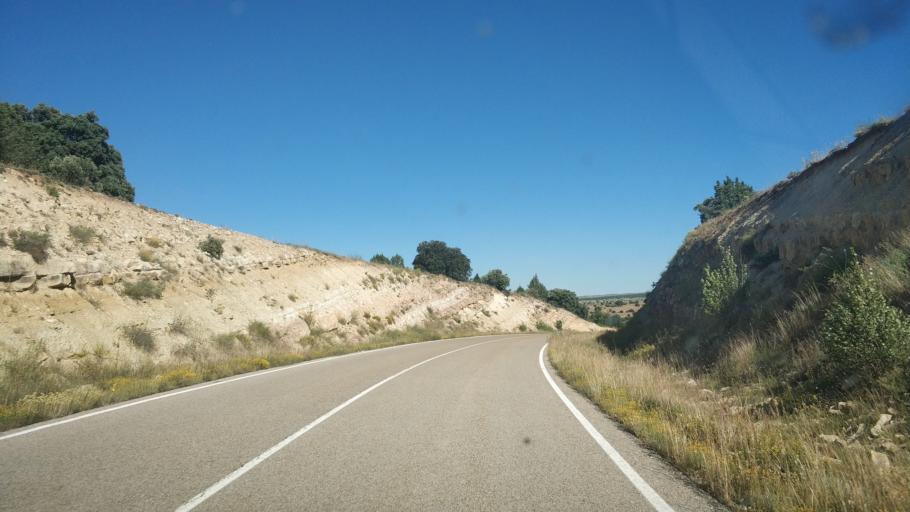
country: ES
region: Castille and Leon
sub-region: Provincia de Soria
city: Montejo de Tiermes
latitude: 41.4022
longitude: -3.2008
